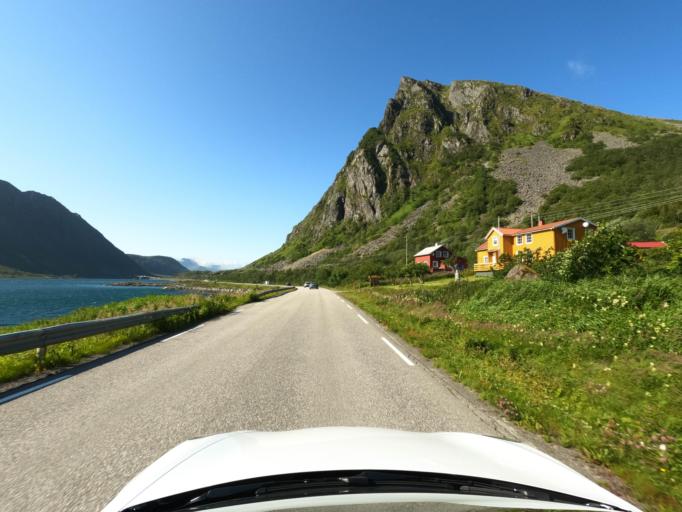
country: NO
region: Nordland
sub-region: Vagan
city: Kabelvag
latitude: 68.2606
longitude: 14.1934
